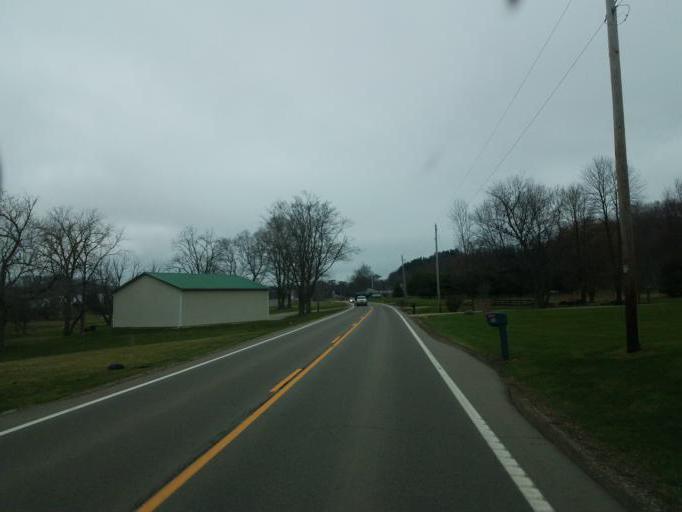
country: US
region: Ohio
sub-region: Ashland County
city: Loudonville
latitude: 40.6872
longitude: -82.2385
